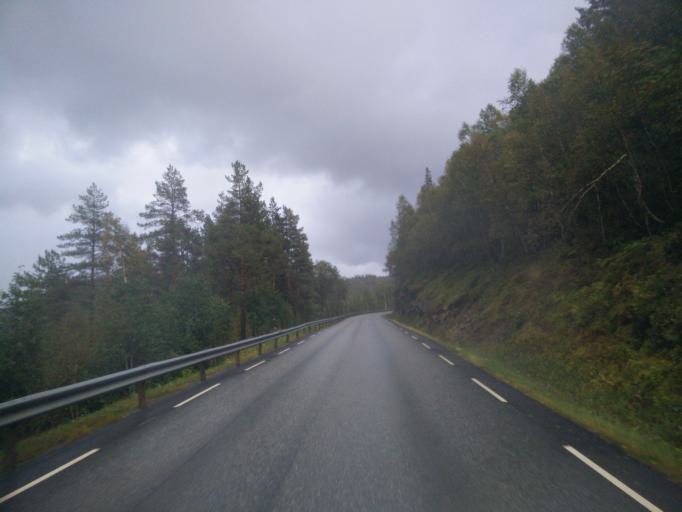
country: NO
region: More og Romsdal
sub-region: Surnadal
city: Surnadal
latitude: 63.0270
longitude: 8.6324
